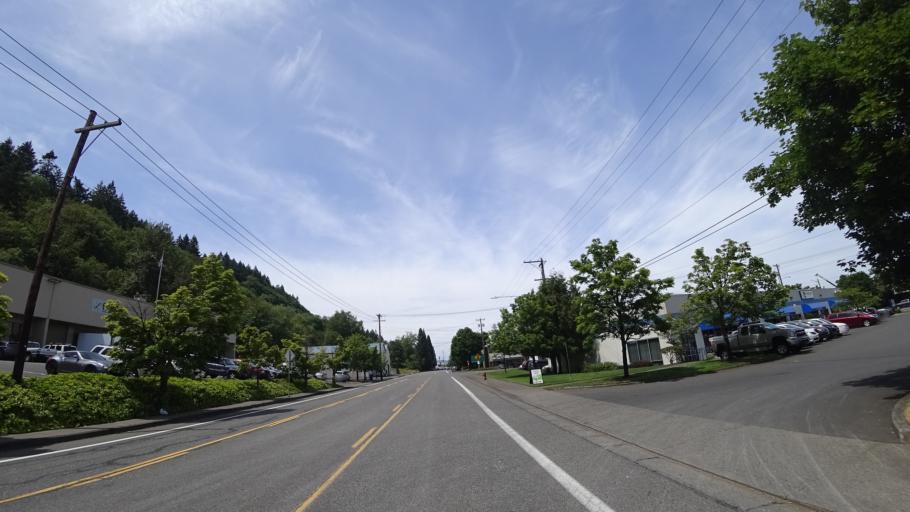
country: US
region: Oregon
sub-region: Washington County
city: West Haven-Sylvan
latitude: 45.5530
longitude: -122.7314
